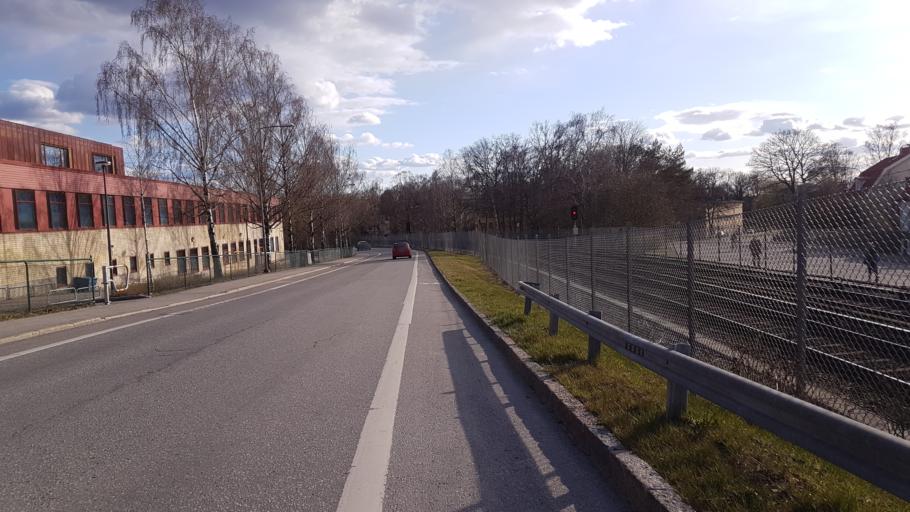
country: SE
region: Stockholm
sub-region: Stockholms Kommun
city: Arsta
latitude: 59.2920
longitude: 18.0709
